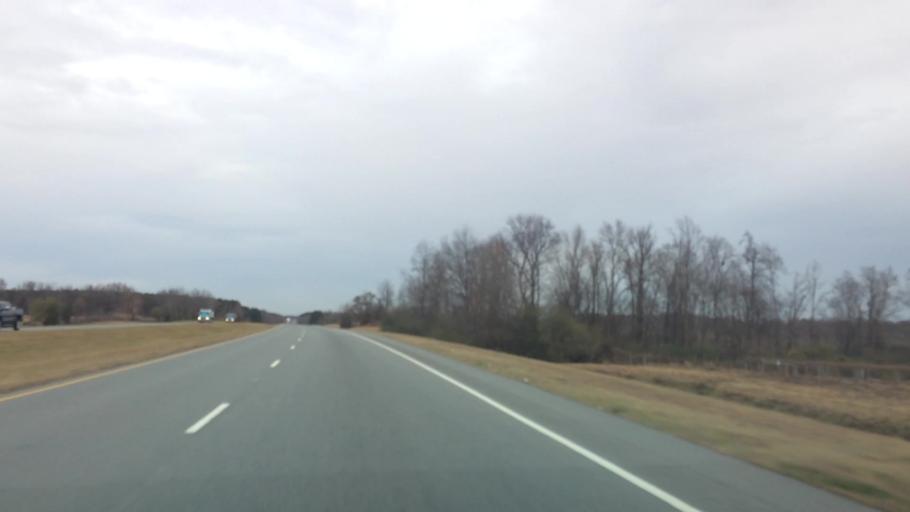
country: US
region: North Carolina
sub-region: Wayne County
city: Mount Olive
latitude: 35.1302
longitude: -78.1467
